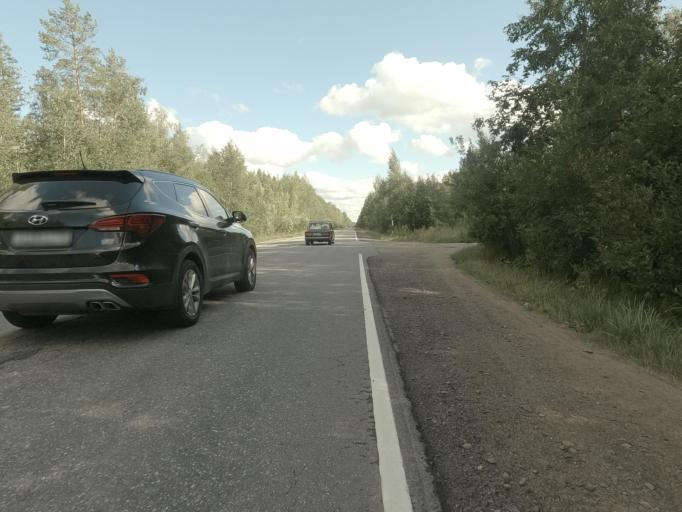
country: RU
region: Leningrad
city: Shcheglovo
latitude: 60.0010
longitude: 30.8701
